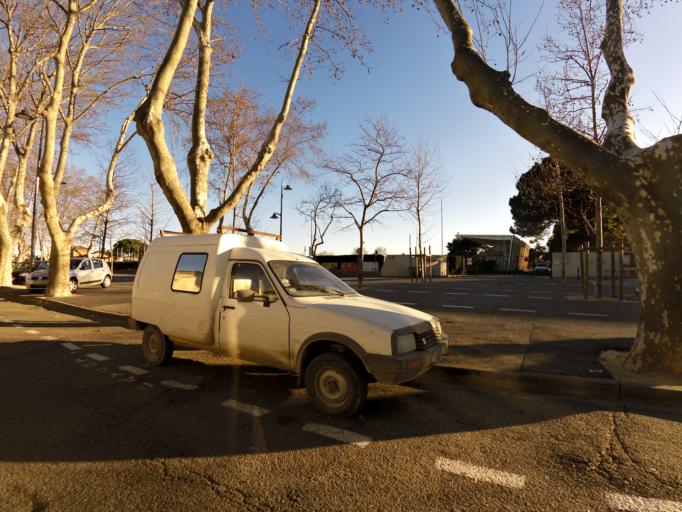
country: FR
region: Languedoc-Roussillon
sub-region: Departement du Gard
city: Aigues-Mortes
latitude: 43.5685
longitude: 4.1959
